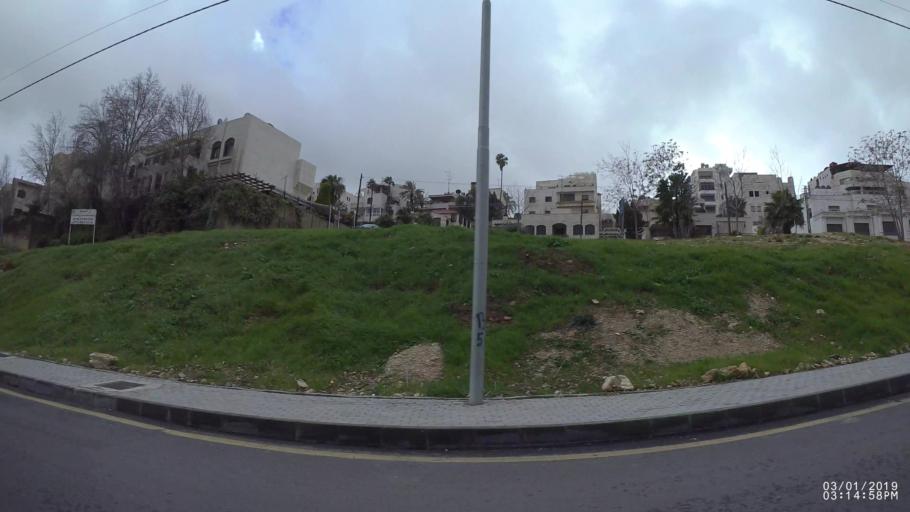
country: JO
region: Amman
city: Amman
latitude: 31.9534
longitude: 35.8891
